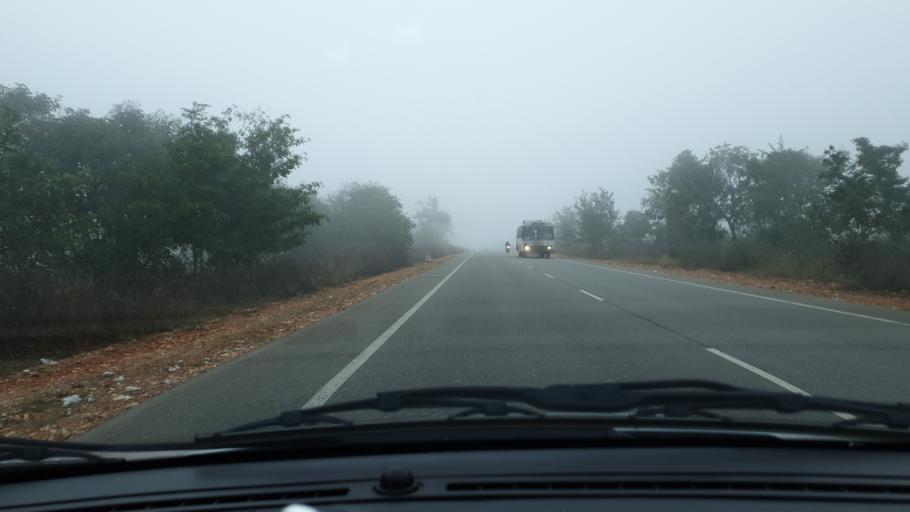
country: IN
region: Telangana
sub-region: Mahbubnagar
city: Nagar Karnul
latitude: 16.6380
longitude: 78.5972
